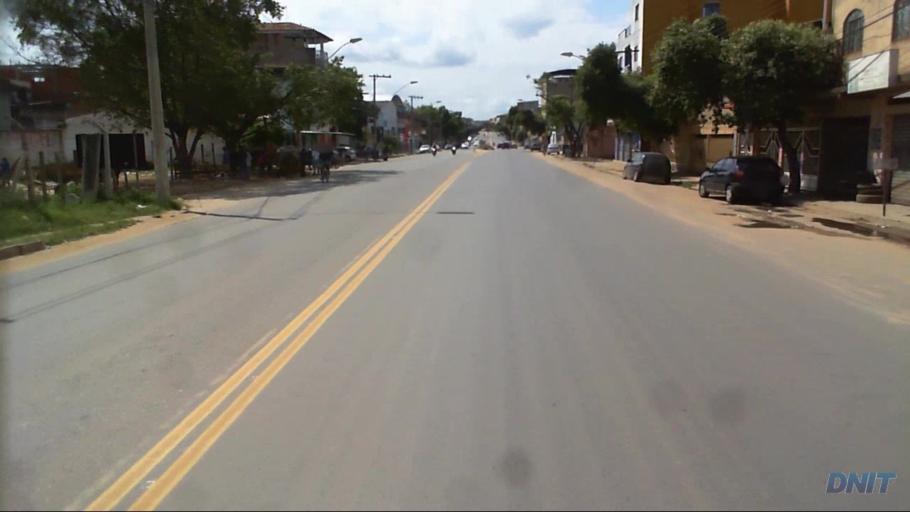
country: BR
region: Minas Gerais
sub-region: Governador Valadares
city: Governador Valadares
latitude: -18.8847
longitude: -41.9683
